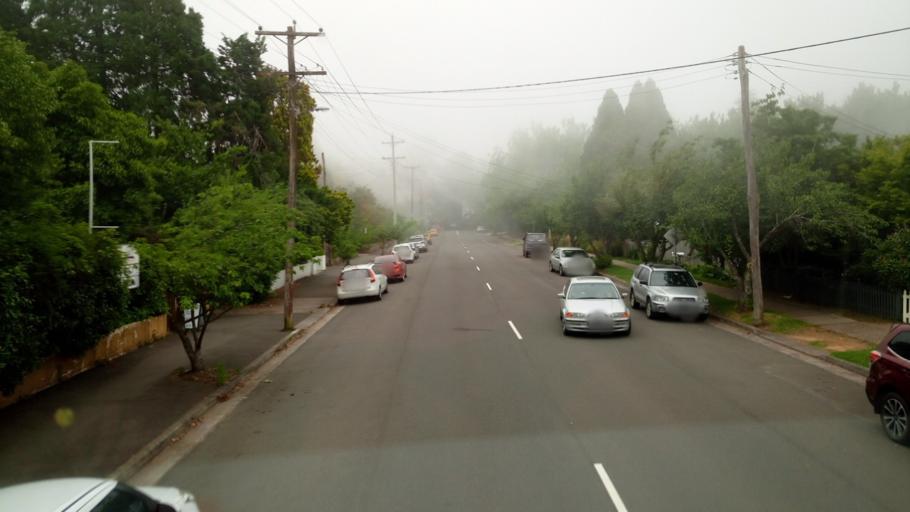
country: AU
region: New South Wales
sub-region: Blue Mountains Municipality
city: Leura
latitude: -33.7138
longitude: 150.3330
